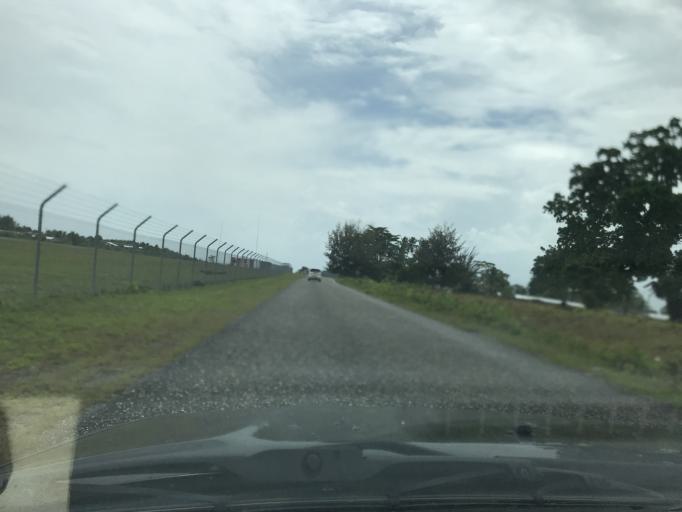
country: SB
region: Western Province
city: Gizo
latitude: -8.3278
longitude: 157.2536
